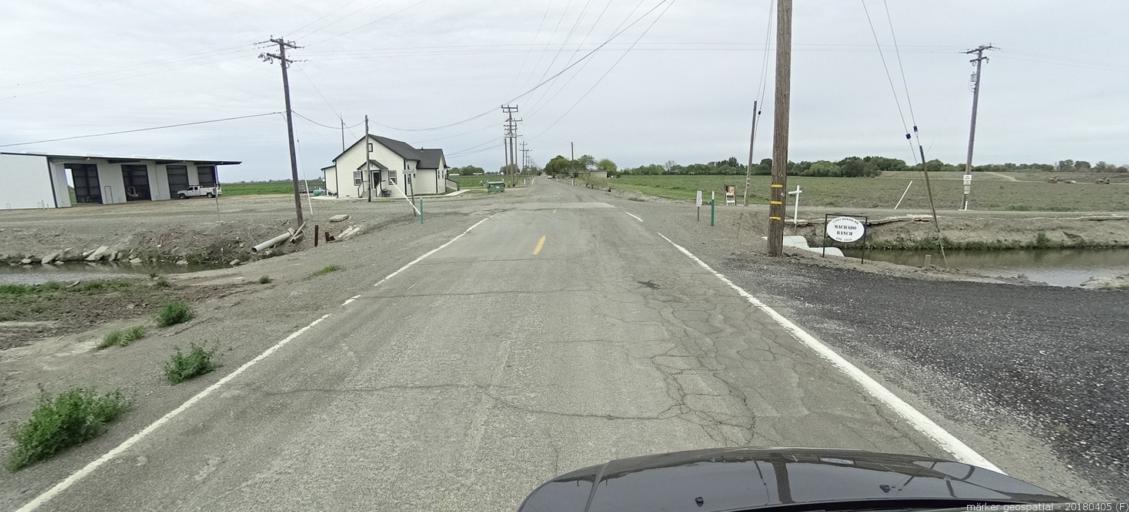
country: US
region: California
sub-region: Sacramento County
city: Walnut Grove
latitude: 38.2985
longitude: -121.5173
